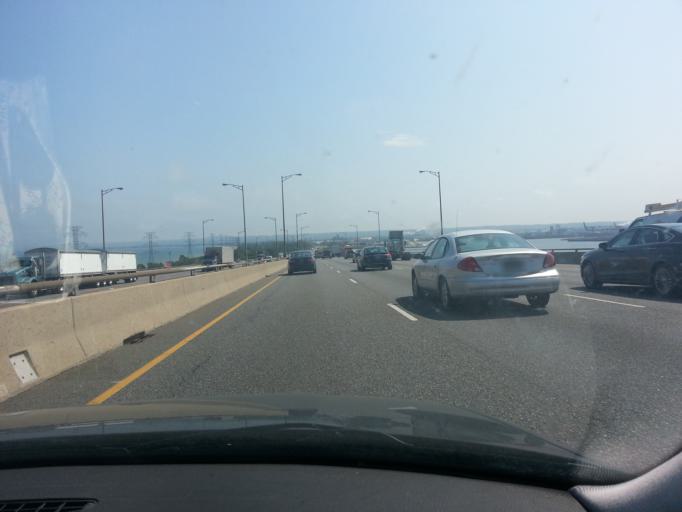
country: CA
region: Ontario
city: Hamilton
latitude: 43.2962
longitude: -79.7959
